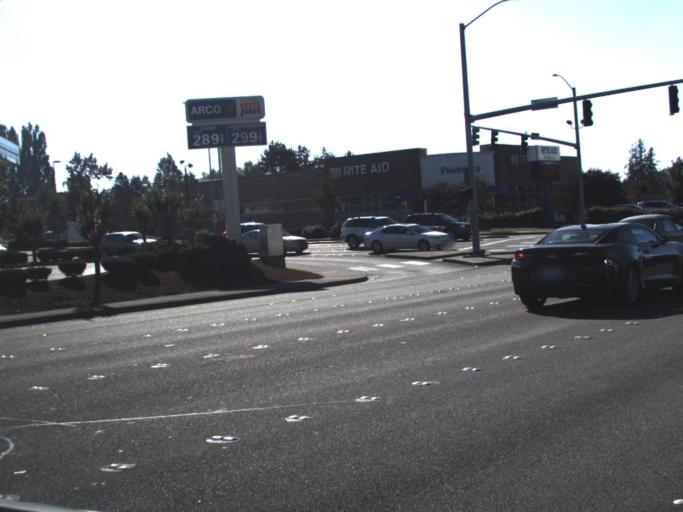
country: US
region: Washington
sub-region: King County
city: Kent
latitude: 47.3730
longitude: -122.2024
